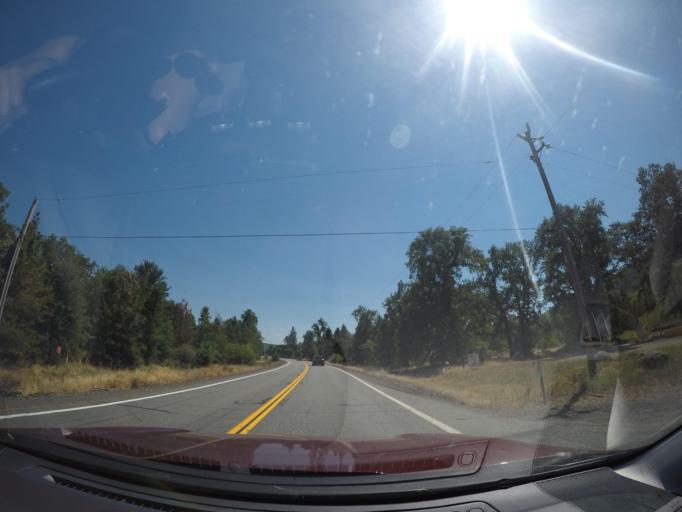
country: US
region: California
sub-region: Shasta County
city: Burney
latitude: 40.8070
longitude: -121.9403
